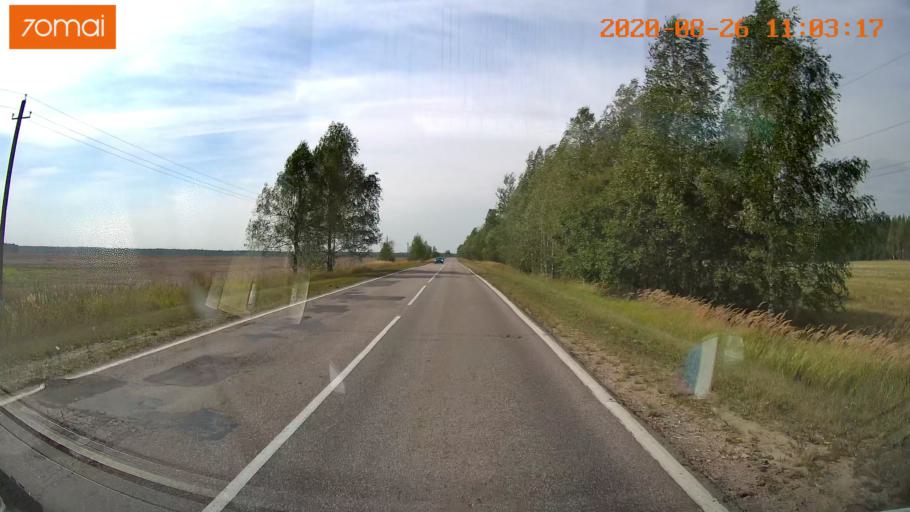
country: RU
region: Rjazan
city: Izhevskoye
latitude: 54.5423
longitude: 41.2137
